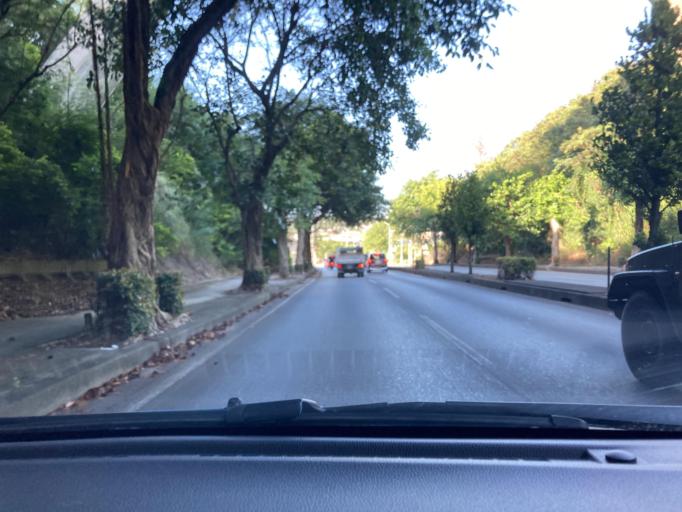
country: JP
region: Okinawa
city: Tomigusuku
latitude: 26.1756
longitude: 127.7127
